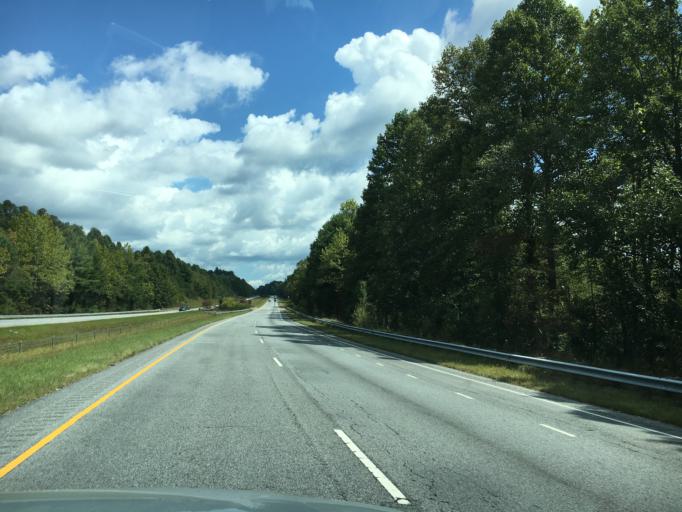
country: US
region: North Carolina
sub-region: Henderson County
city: Flat Rock
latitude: 35.2215
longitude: -82.4409
